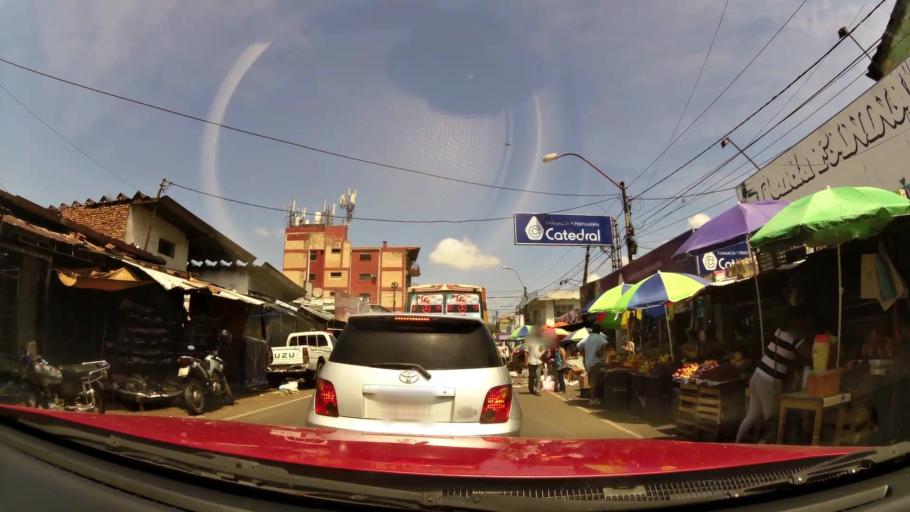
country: PY
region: Central
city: San Lorenzo
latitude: -25.3454
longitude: -57.5115
